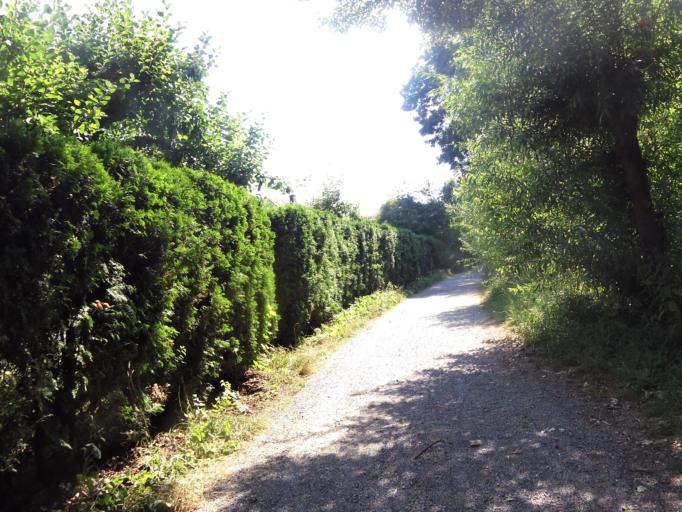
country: DE
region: Bavaria
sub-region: Regierungsbezirk Unterfranken
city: Estenfeld
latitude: 49.8121
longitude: 9.9891
